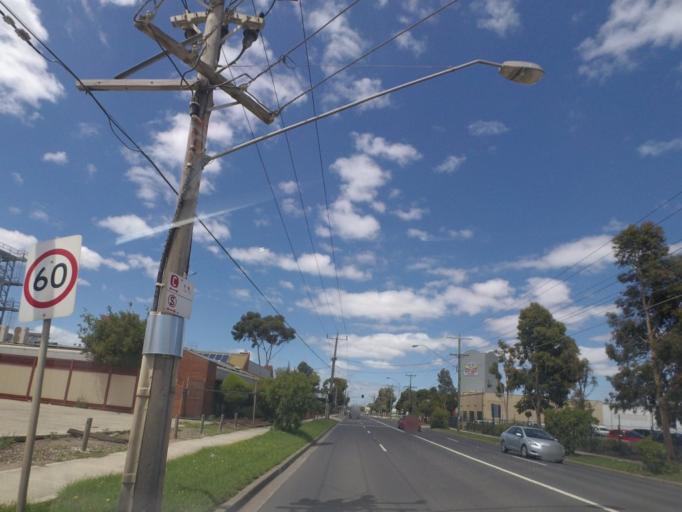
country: AU
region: Victoria
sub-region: Brimbank
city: Sunshine North
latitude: -37.7740
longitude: 144.8294
